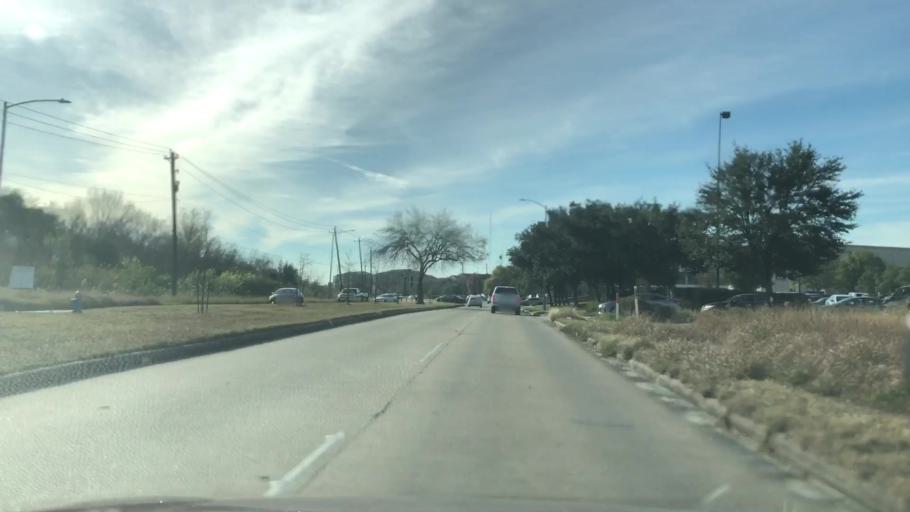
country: US
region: Texas
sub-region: Fort Bend County
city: Missouri City
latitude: 29.6243
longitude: -95.4953
